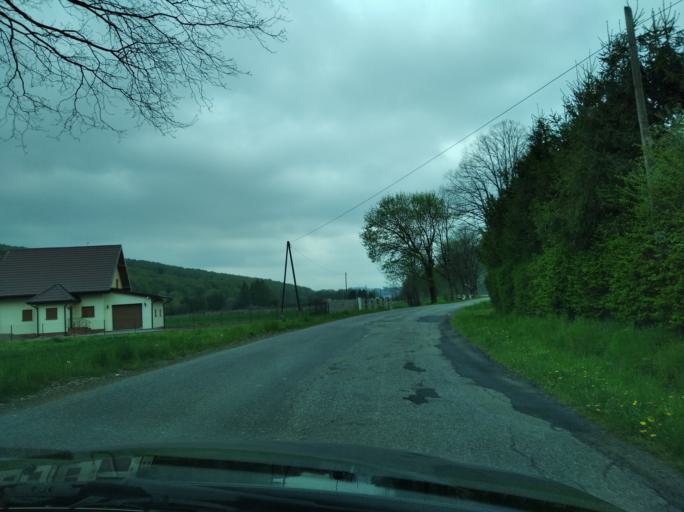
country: PL
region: Subcarpathian Voivodeship
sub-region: Powiat sanocki
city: Sanok
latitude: 49.6139
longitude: 22.2614
